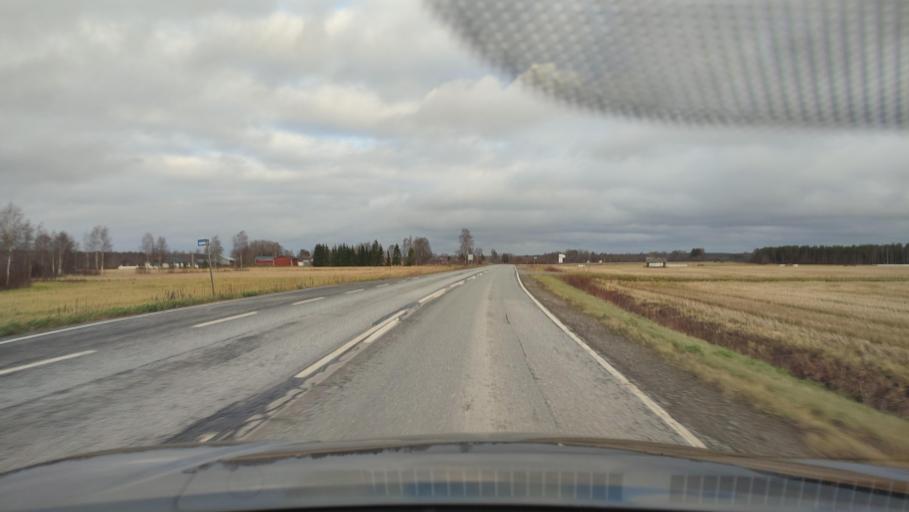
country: FI
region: Southern Ostrobothnia
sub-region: Suupohja
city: Kauhajoki
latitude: 62.3725
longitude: 22.0795
